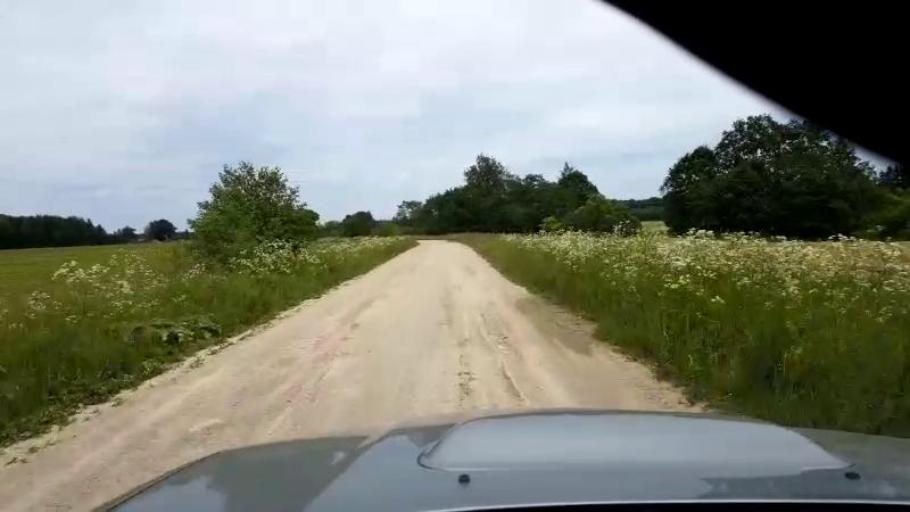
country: EE
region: Paernumaa
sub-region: Sindi linn
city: Sindi
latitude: 58.5156
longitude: 24.6105
